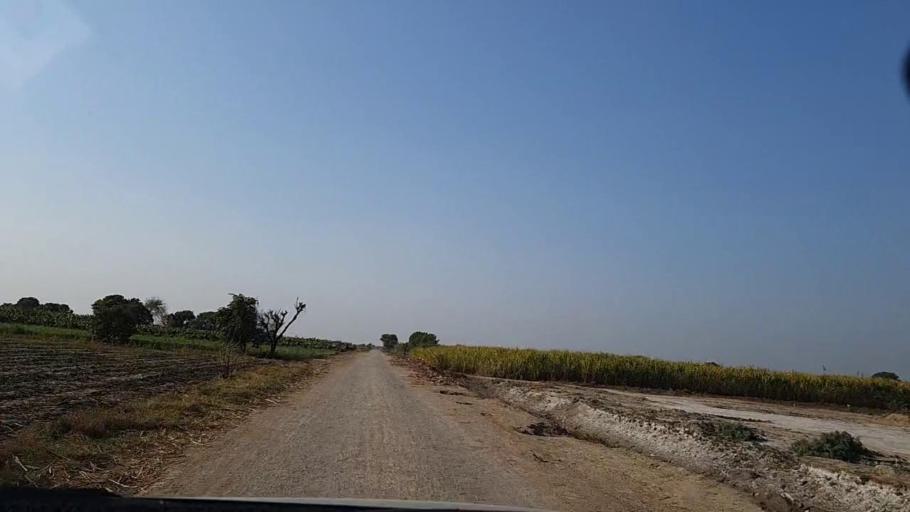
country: PK
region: Sindh
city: Mirwah Gorchani
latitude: 25.2264
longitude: 68.9863
